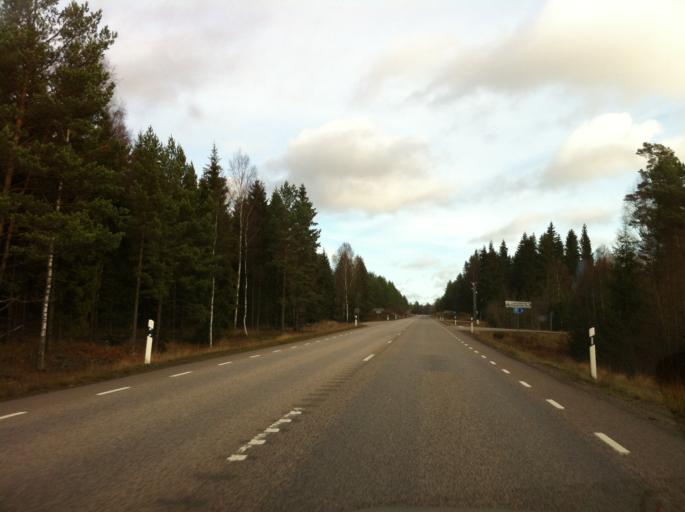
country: SE
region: Kronoberg
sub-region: Uppvidinge Kommun
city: Lenhovda
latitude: 57.1034
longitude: 15.2061
